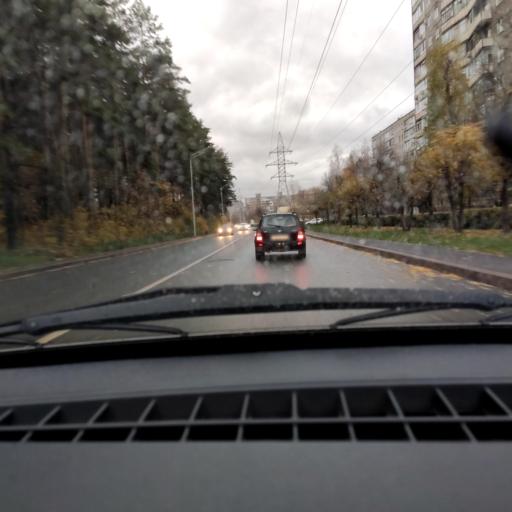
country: RU
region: Bashkortostan
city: Ufa
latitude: 54.7060
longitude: 56.0081
